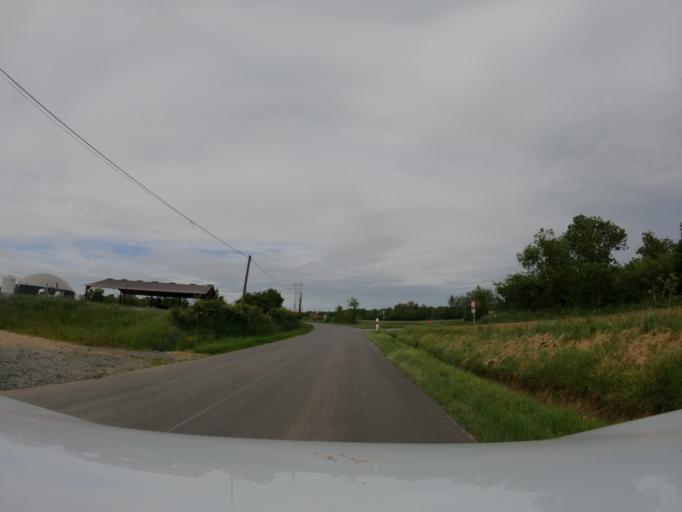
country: FR
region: Pays de la Loire
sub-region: Departement de la Vendee
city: Saint-Hilaire-des-Loges
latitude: 46.5068
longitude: -0.6475
